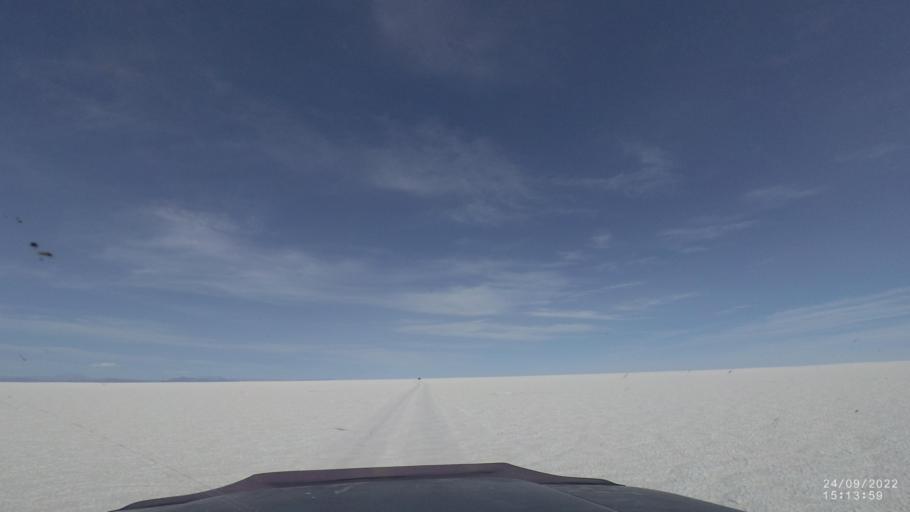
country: BO
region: Potosi
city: Colchani
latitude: -19.9601
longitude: -67.4599
